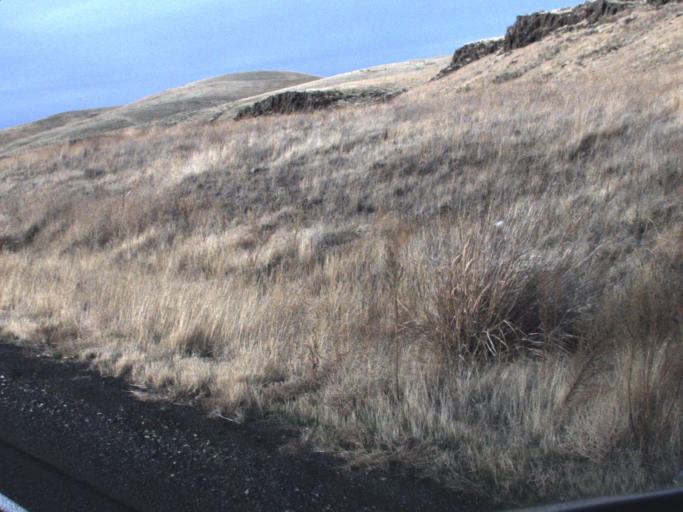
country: US
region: Washington
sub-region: Garfield County
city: Pomeroy
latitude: 46.4681
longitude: -117.7130
